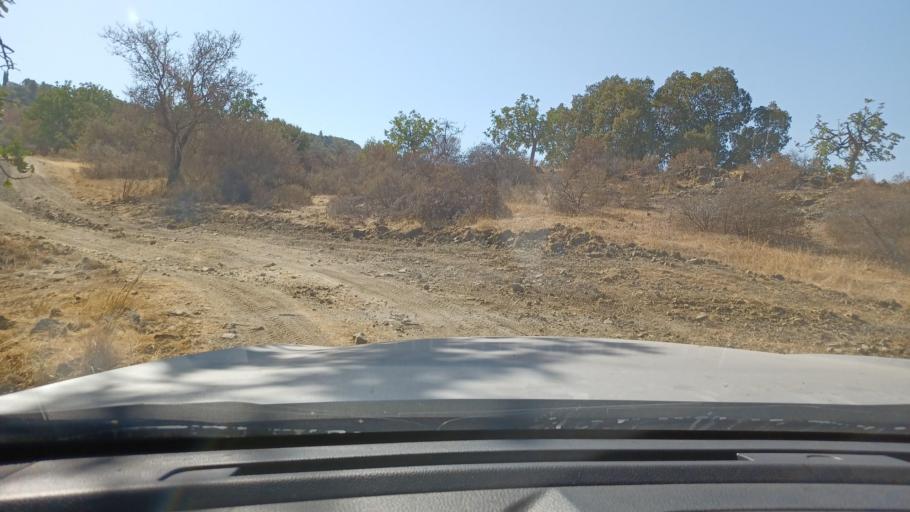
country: CY
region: Pafos
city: Polis
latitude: 35.0016
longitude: 32.5037
